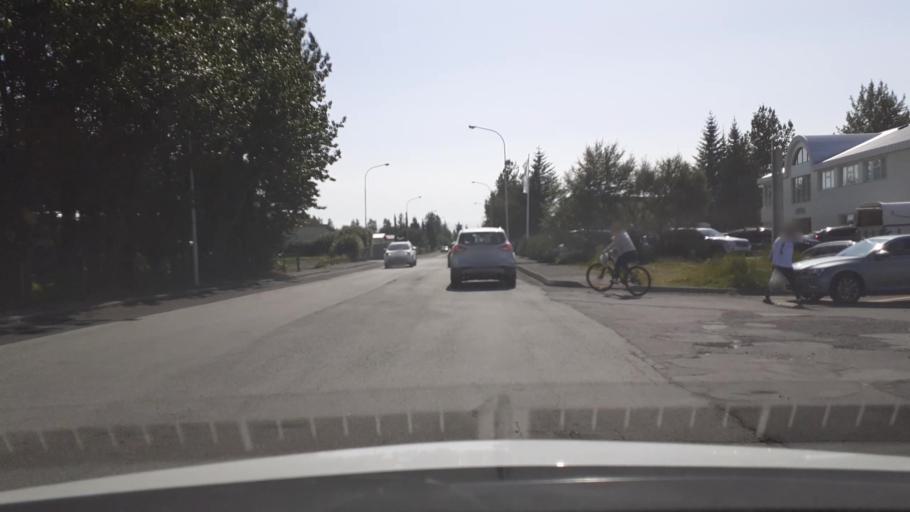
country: IS
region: South
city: Selfoss
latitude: 63.9367
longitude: -20.9871
